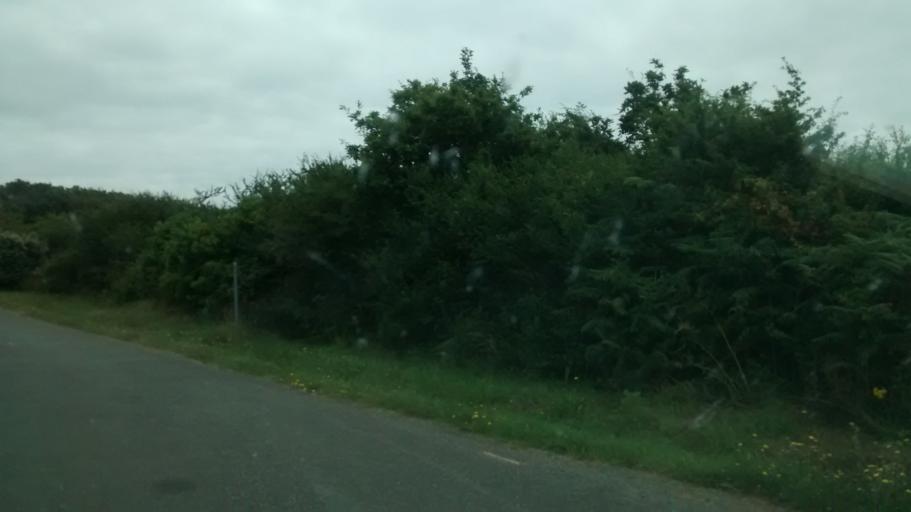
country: FR
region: Brittany
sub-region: Departement du Finistere
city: Lanveoc
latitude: 48.3316
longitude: -4.4368
